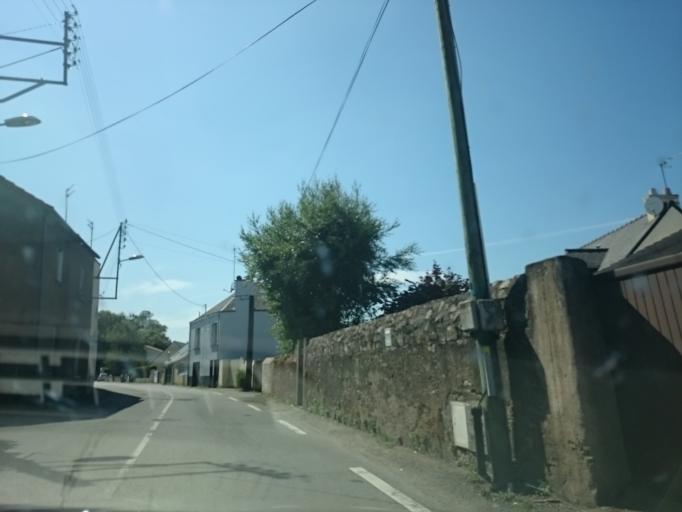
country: FR
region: Pays de la Loire
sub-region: Departement de la Loire-Atlantique
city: Coueron
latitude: 47.2112
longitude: -1.7318
